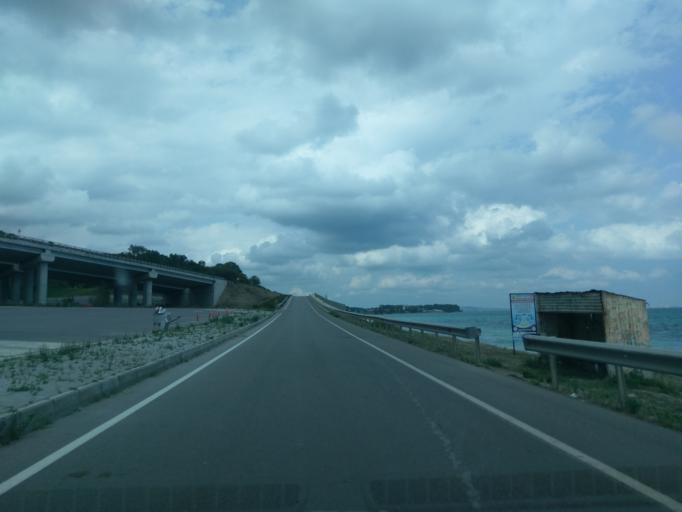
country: TR
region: Sinop
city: Gerze
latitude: 41.8238
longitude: 35.1684
